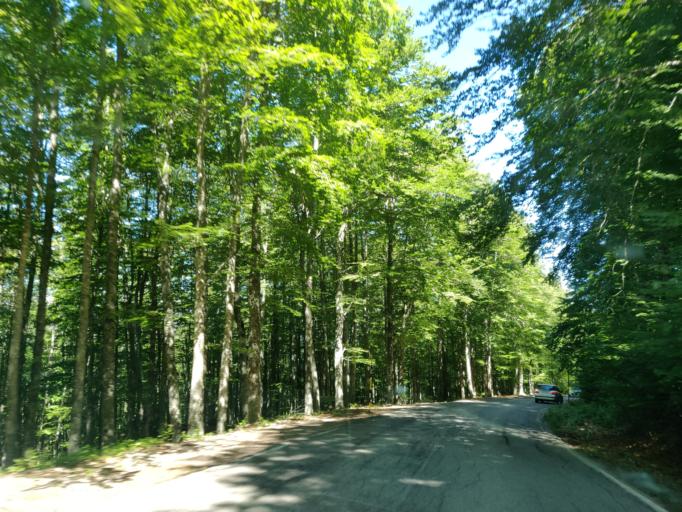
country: IT
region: Tuscany
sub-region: Provincia di Siena
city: Abbadia San Salvatore
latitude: 42.8959
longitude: 11.6134
